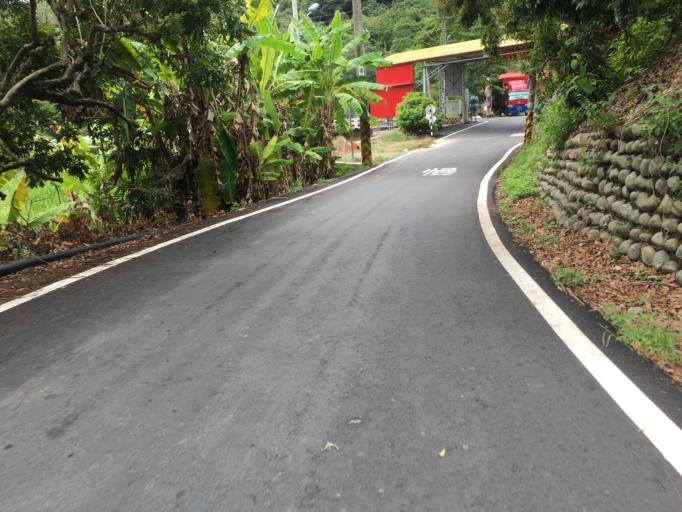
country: TW
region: Taiwan
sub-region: Taichung City
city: Taichung
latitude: 24.0625
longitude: 120.7392
